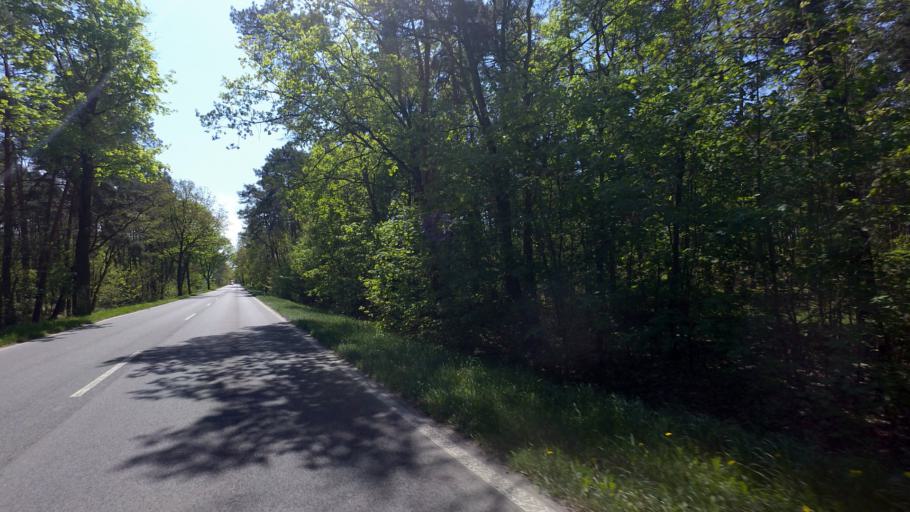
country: DE
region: Brandenburg
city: Bestensee
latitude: 52.2522
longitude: 13.6562
